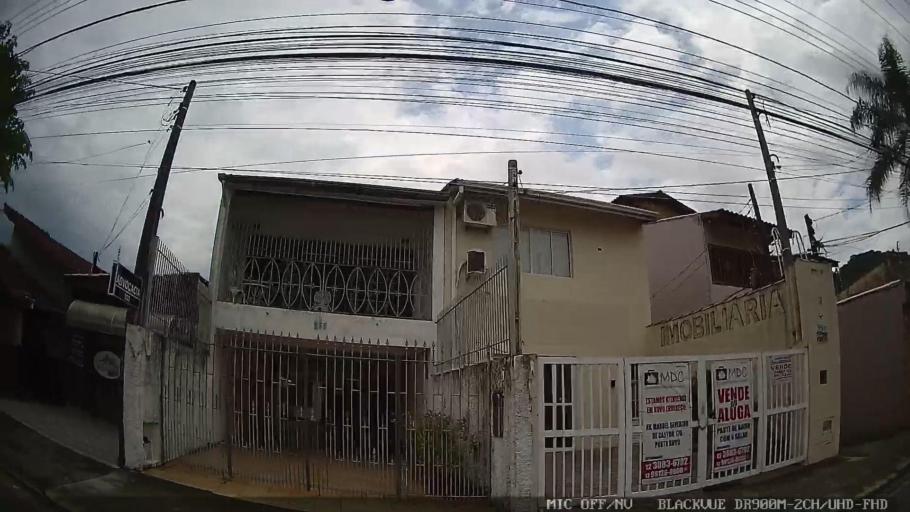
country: BR
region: Sao Paulo
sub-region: Caraguatatuba
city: Caraguatatuba
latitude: -23.6193
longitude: -45.4071
